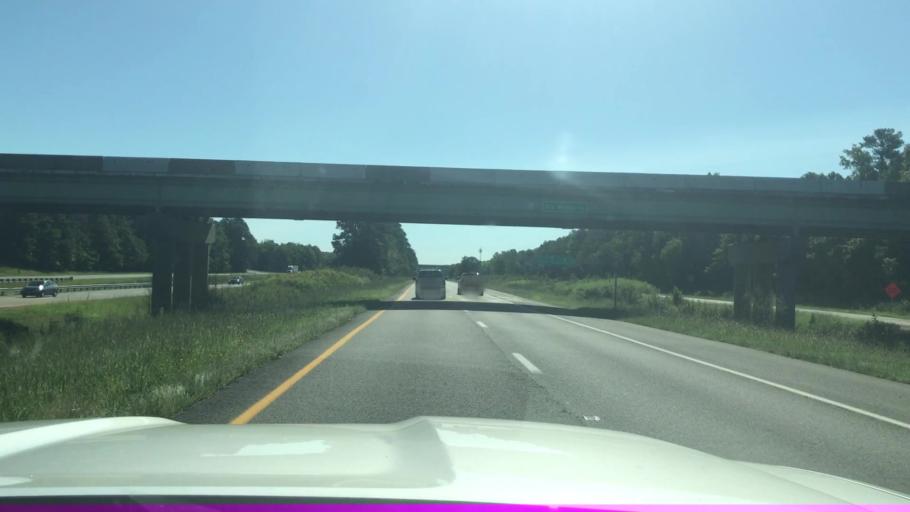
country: US
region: Virginia
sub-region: Henrico County
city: Sandston
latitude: 37.5237
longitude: -77.2815
